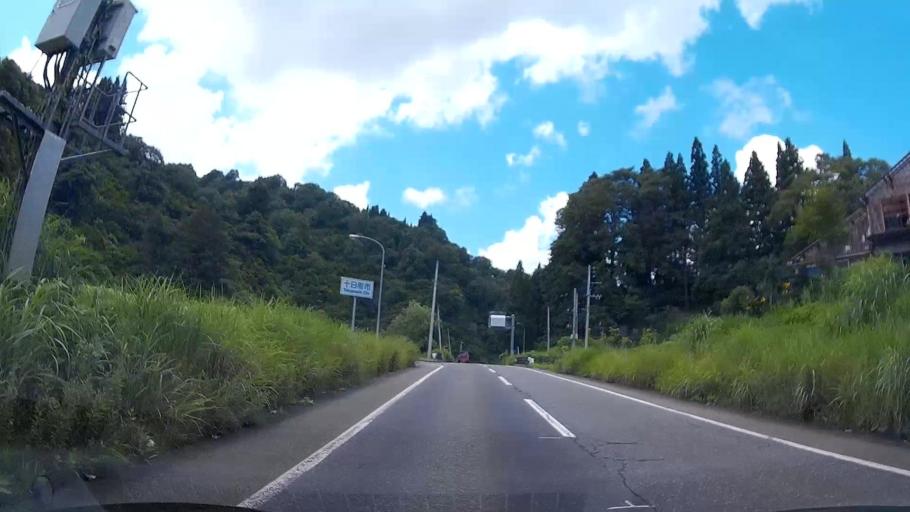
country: JP
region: Niigata
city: Shiozawa
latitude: 37.0402
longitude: 138.7771
